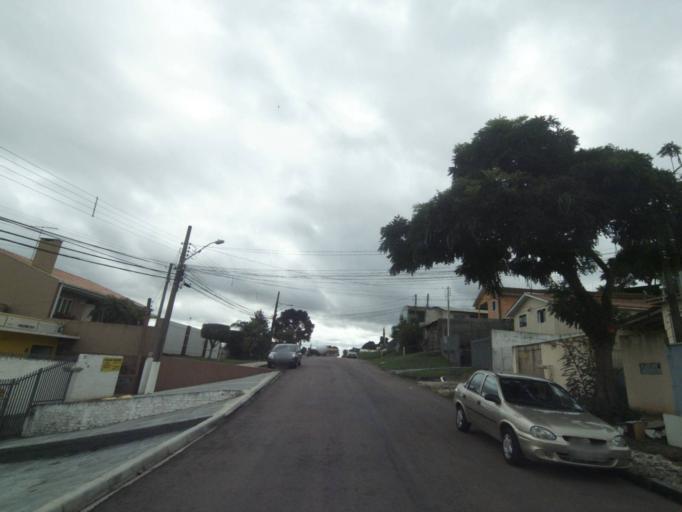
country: BR
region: Parana
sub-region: Curitiba
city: Curitiba
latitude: -25.4766
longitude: -49.2702
